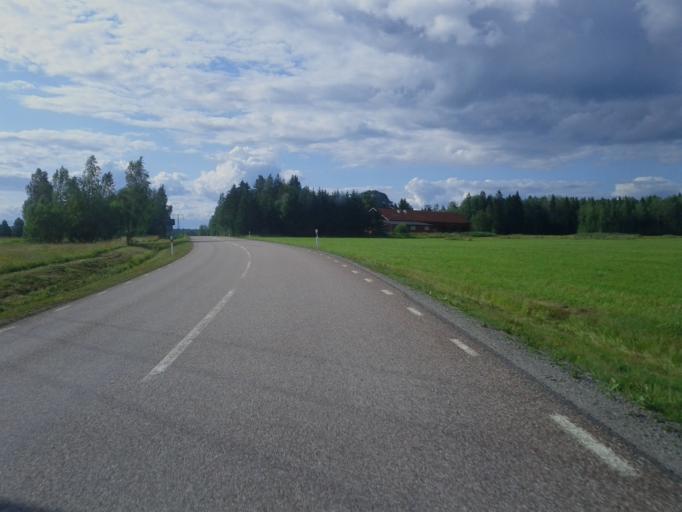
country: SE
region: Vaestmanland
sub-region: Sala Kommun
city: Sala
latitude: 59.9147
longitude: 16.5178
